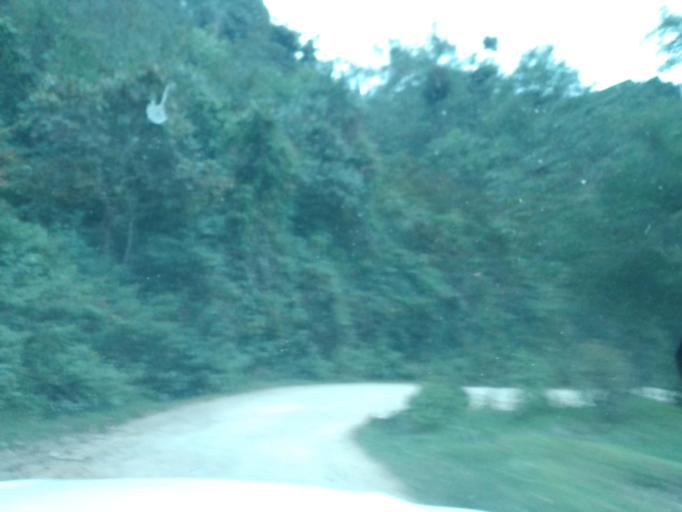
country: MX
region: Chiapas
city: Motozintla de Mendoza
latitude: 15.2170
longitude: -92.2394
